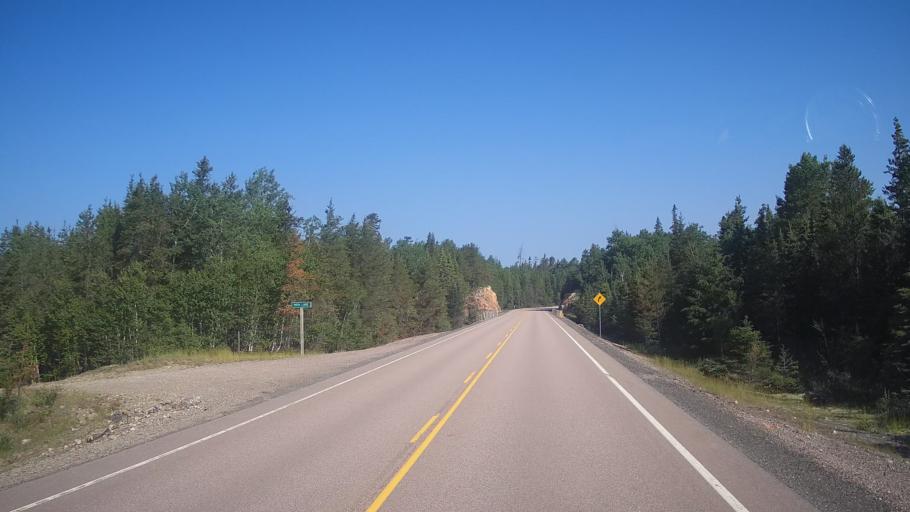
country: CA
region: Ontario
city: Rayside-Balfour
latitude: 46.9792
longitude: -81.6320
